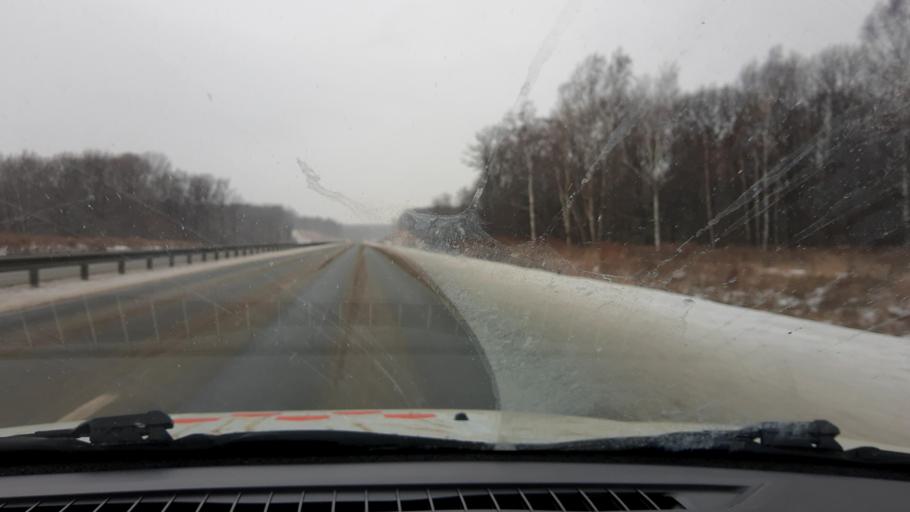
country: RU
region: Nizjnij Novgorod
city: Kstovo
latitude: 56.1008
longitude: 44.0418
